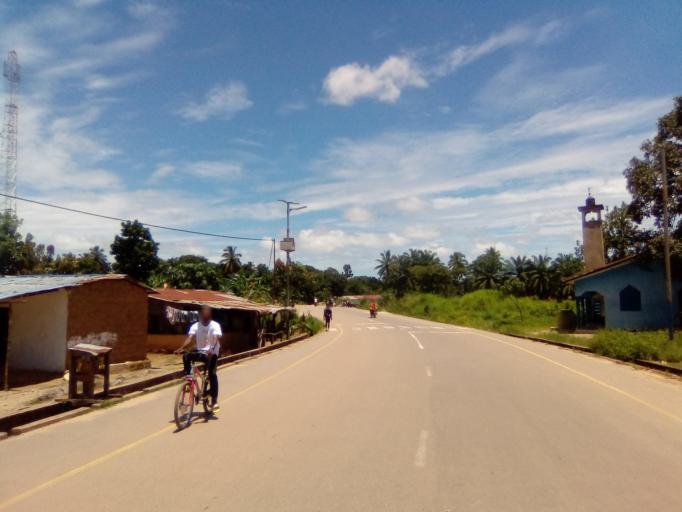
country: SL
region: Eastern Province
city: Koidu
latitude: 8.6387
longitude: -10.9681
